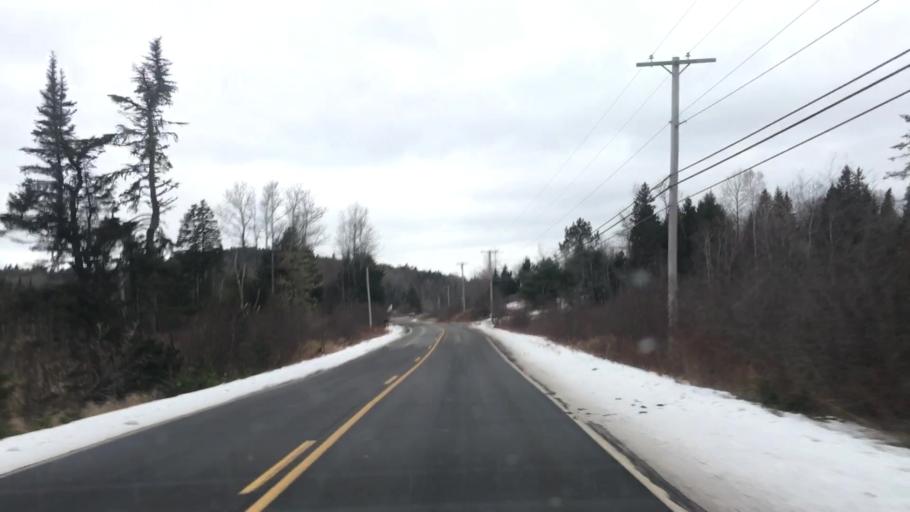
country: US
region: Maine
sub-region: Washington County
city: Machiasport
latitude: 44.7077
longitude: -67.3640
